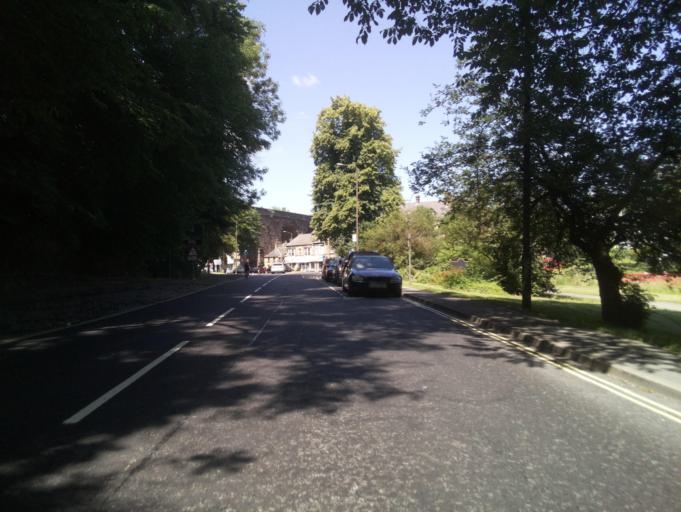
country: GB
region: England
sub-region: Derbyshire
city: Buxton
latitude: 53.2586
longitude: -1.9055
